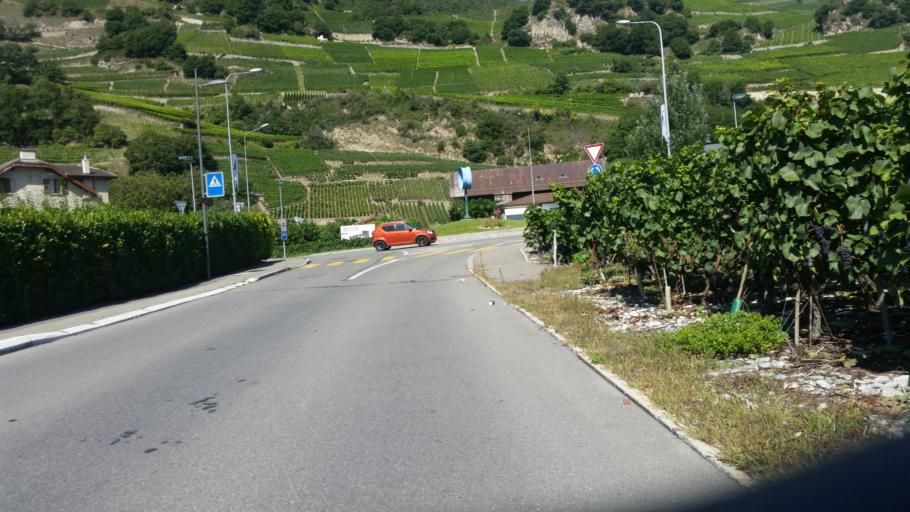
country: CH
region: Valais
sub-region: Martigny District
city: Saillon
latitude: 46.1760
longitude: 7.1923
